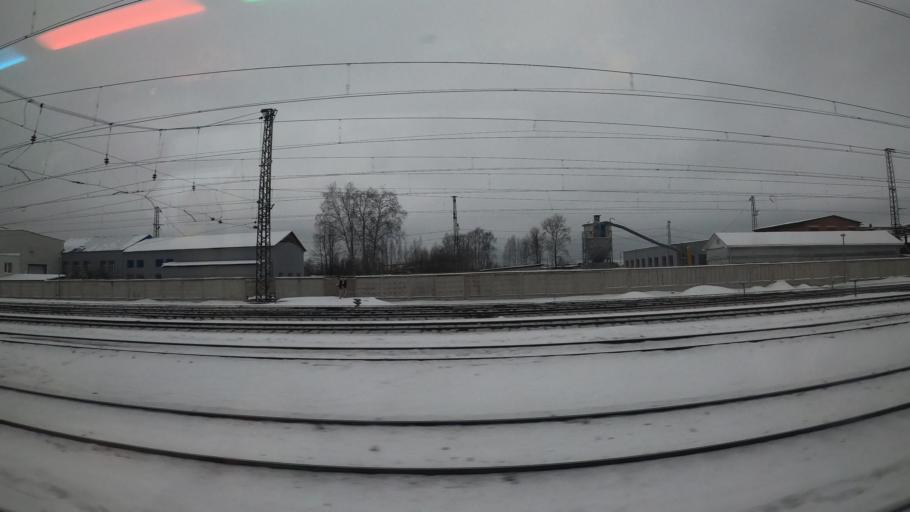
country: RU
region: Vladimir
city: Aleksandrov
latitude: 56.3993
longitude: 38.7058
